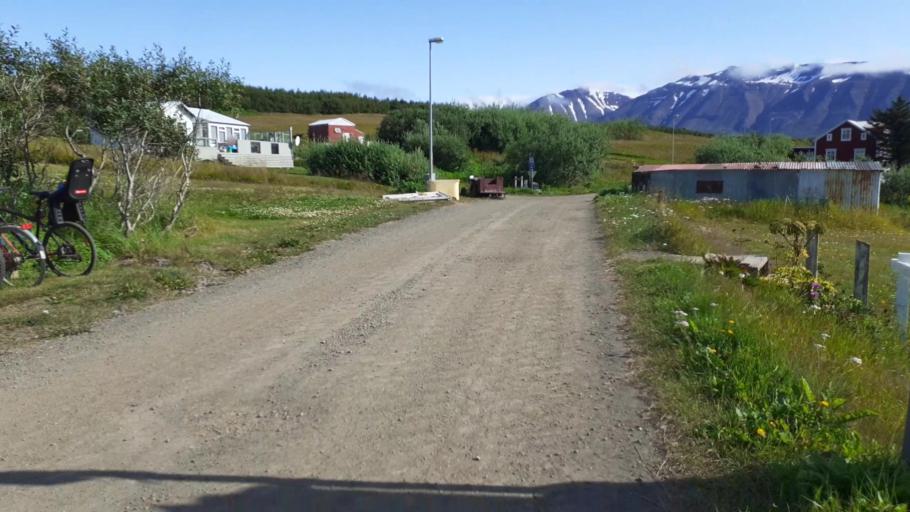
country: IS
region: Northeast
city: Dalvik
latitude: 65.9790
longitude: -18.3633
